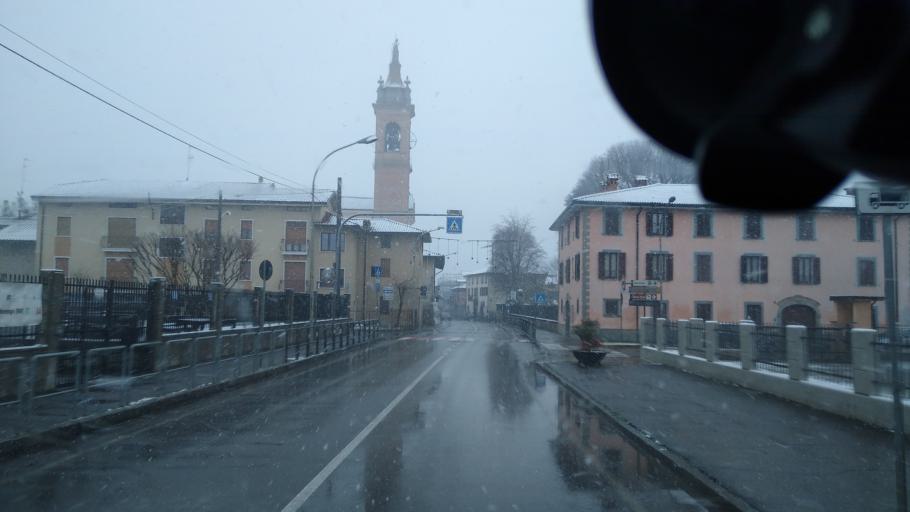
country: IT
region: Lombardy
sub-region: Provincia di Bergamo
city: Morengo
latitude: 45.5353
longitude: 9.7053
